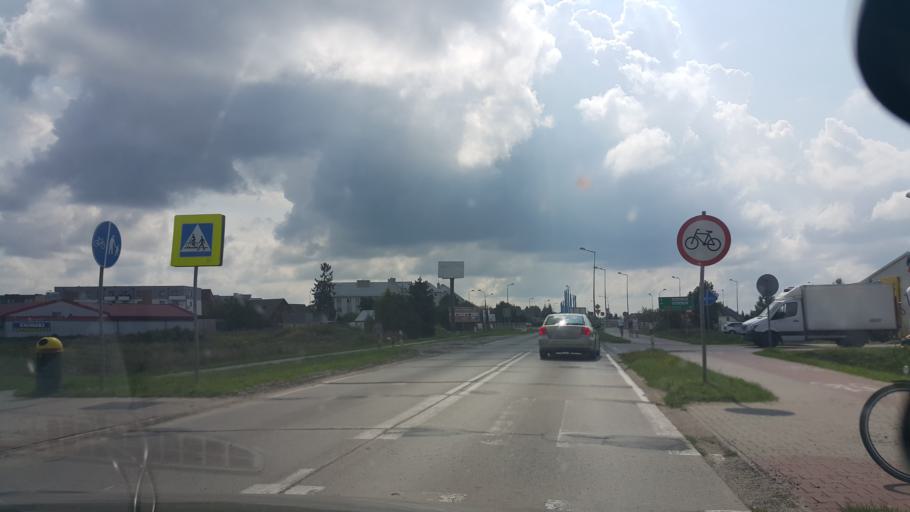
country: PL
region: Lublin Voivodeship
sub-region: Powiat wlodawski
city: Wlodawa
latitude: 51.5480
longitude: 23.5418
